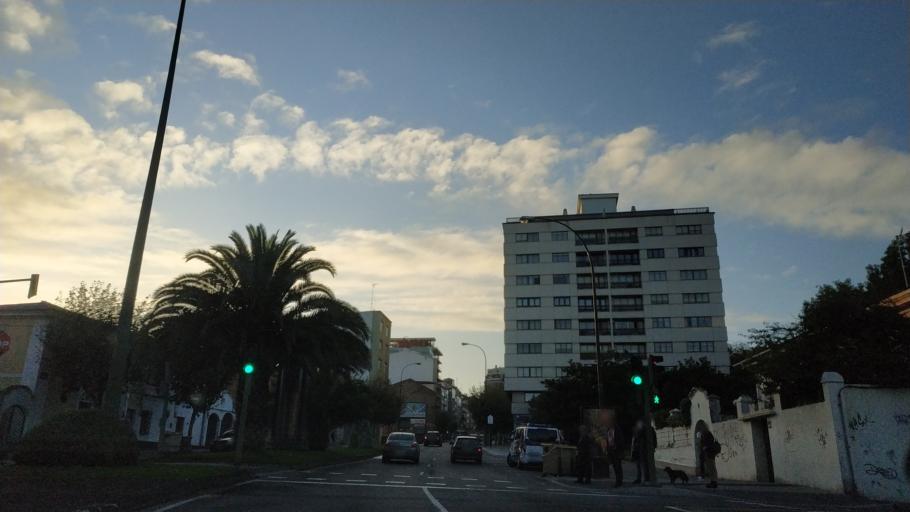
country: ES
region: Galicia
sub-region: Provincia da Coruna
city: A Coruna
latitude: 43.3593
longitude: -8.4119
